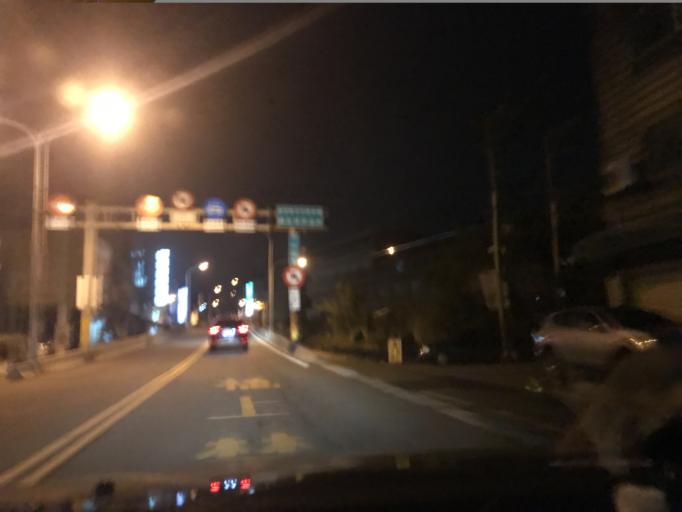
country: TW
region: Taiwan
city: Taoyuan City
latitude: 24.9591
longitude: 121.2328
